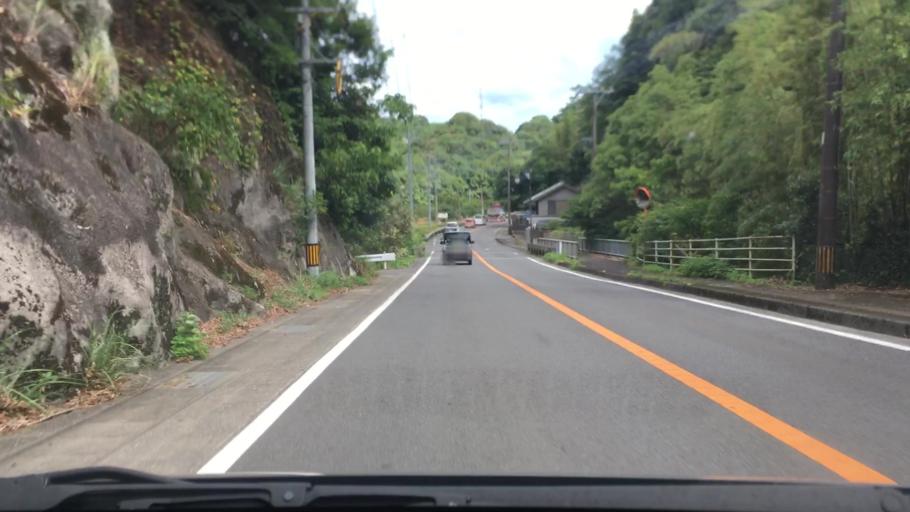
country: JP
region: Nagasaki
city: Togitsu
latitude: 32.9564
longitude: 129.7837
